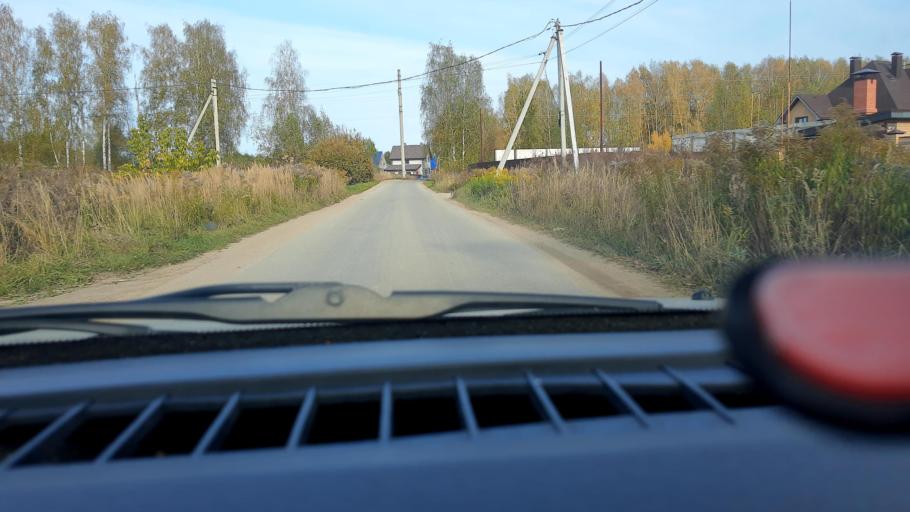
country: RU
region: Nizjnij Novgorod
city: Afonino
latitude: 56.2992
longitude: 44.1978
